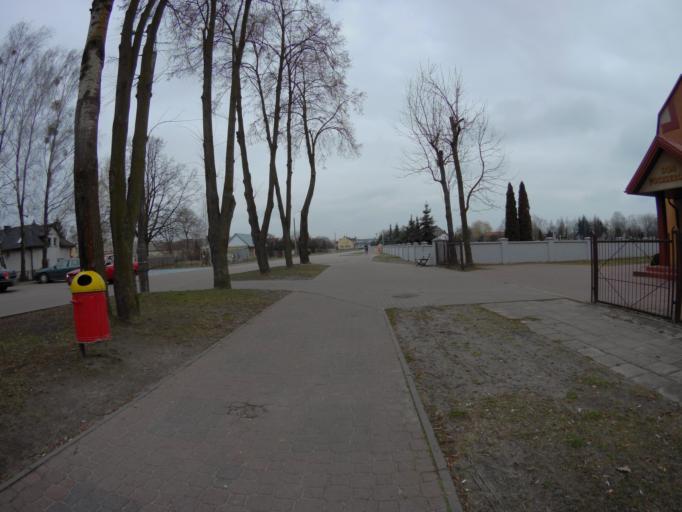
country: PL
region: Lublin Voivodeship
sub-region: Powiat bialski
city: Terespol
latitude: 52.0750
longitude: 23.6079
